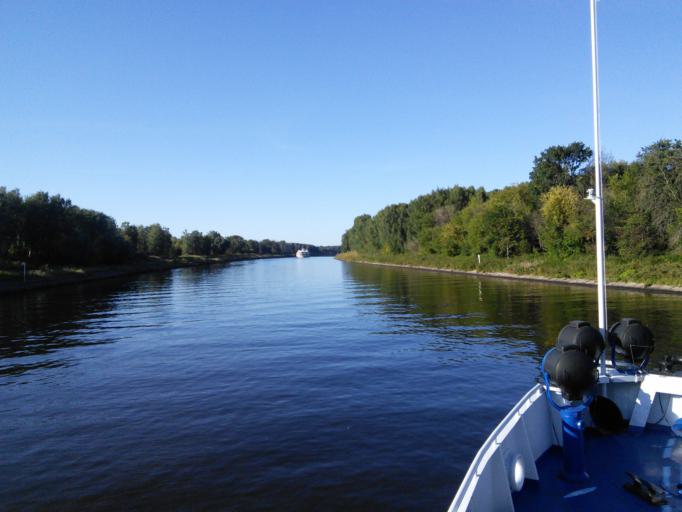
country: RU
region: Moskovskaya
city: Yakhroma
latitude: 56.2995
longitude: 37.4896
